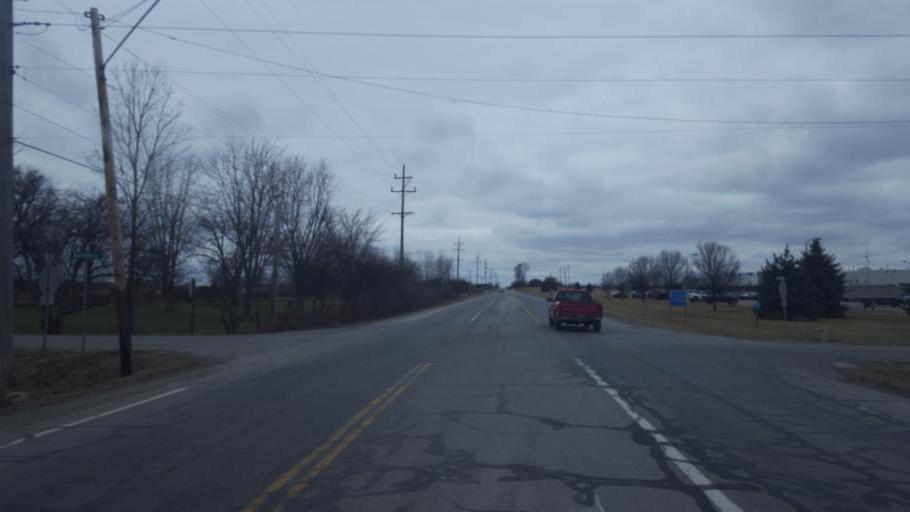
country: US
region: Ohio
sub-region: Crawford County
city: Crestline
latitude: 40.7863
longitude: -82.6972
